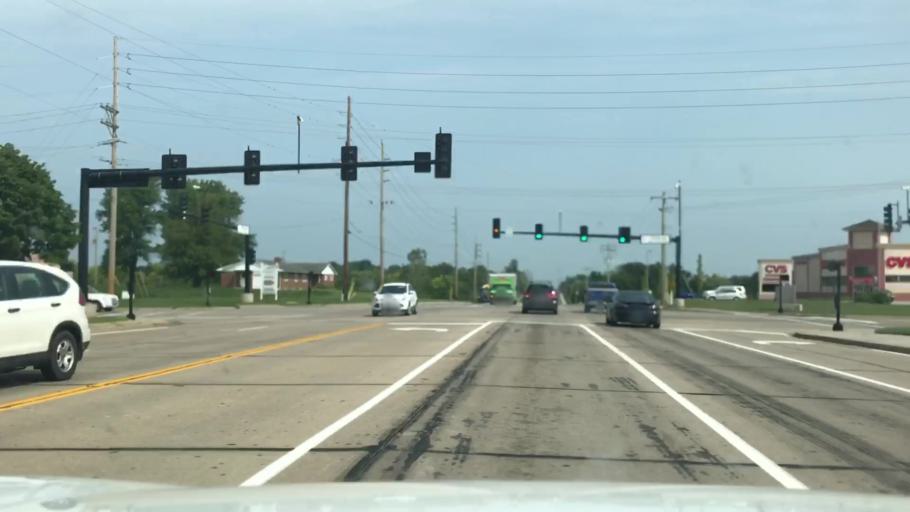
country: US
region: Missouri
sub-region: Saint Charles County
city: Dardenne Prairie
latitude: 38.7728
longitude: -90.7375
